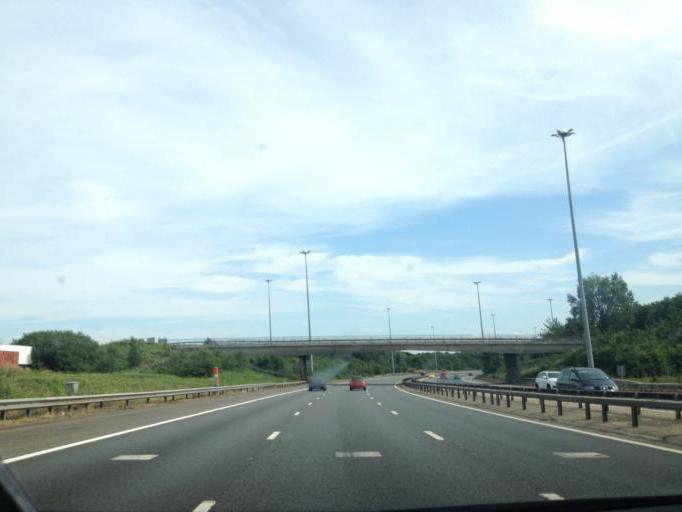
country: GB
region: England
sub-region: Hertfordshire
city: Borehamwood
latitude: 51.6357
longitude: -0.2665
